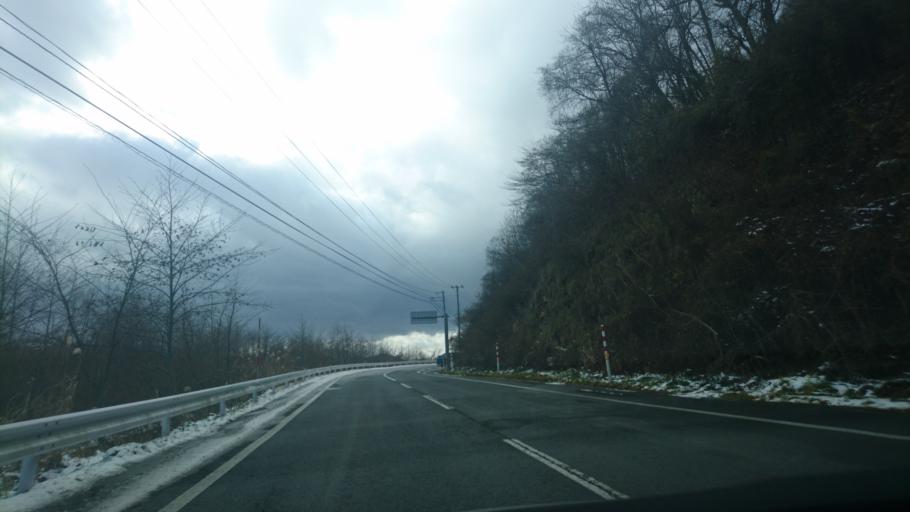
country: JP
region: Iwate
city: Mizusawa
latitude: 39.1727
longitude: 141.3461
